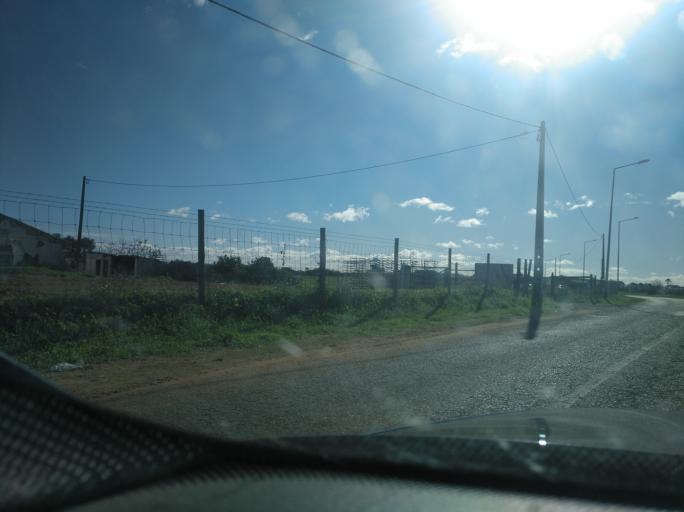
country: PT
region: Faro
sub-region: Vila Real de Santo Antonio
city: Monte Gordo
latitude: 37.1765
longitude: -7.5203
